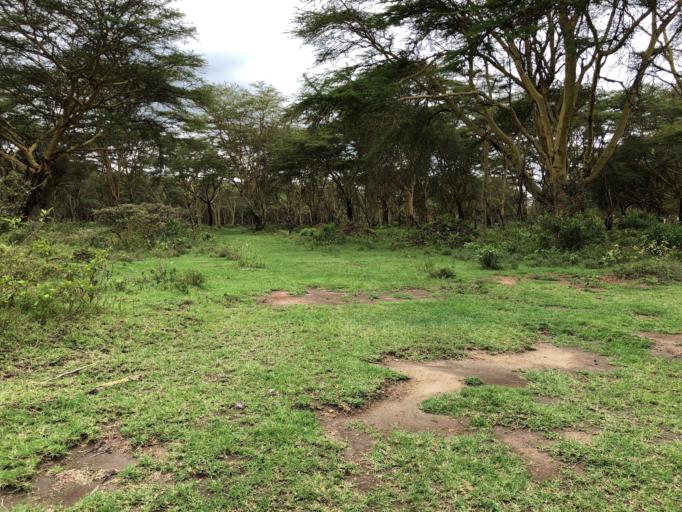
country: KE
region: Nakuru
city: Naivasha
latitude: -0.7424
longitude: 36.4299
